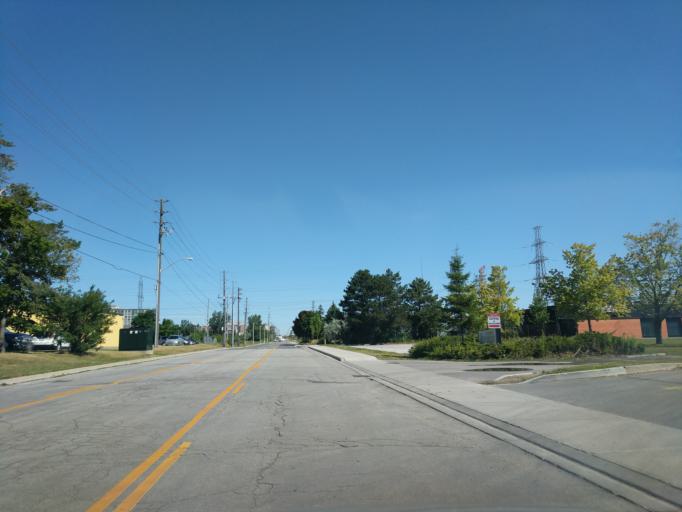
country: CA
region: Ontario
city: Scarborough
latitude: 43.8083
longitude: -79.2972
